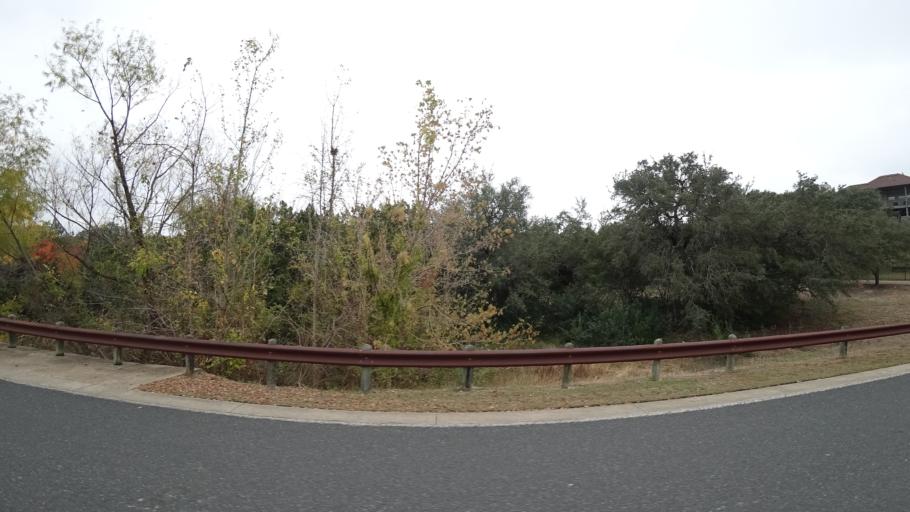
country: US
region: Texas
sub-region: Williamson County
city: Anderson Mill
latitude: 30.4460
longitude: -97.8230
